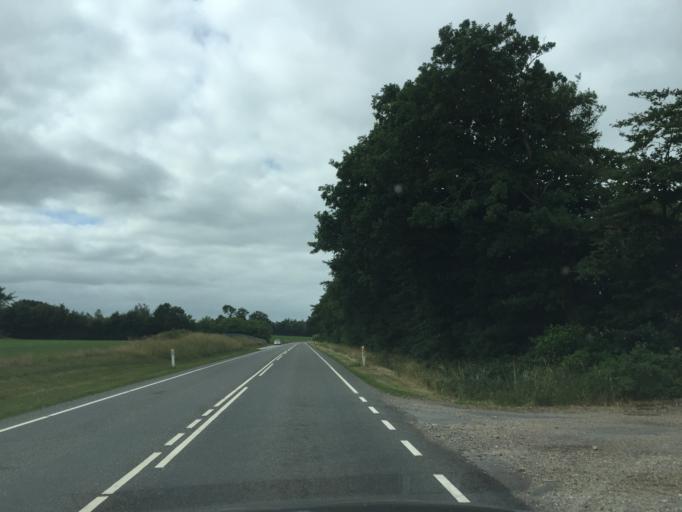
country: DK
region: South Denmark
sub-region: Vejen Kommune
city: Brorup
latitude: 55.4214
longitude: 8.9559
